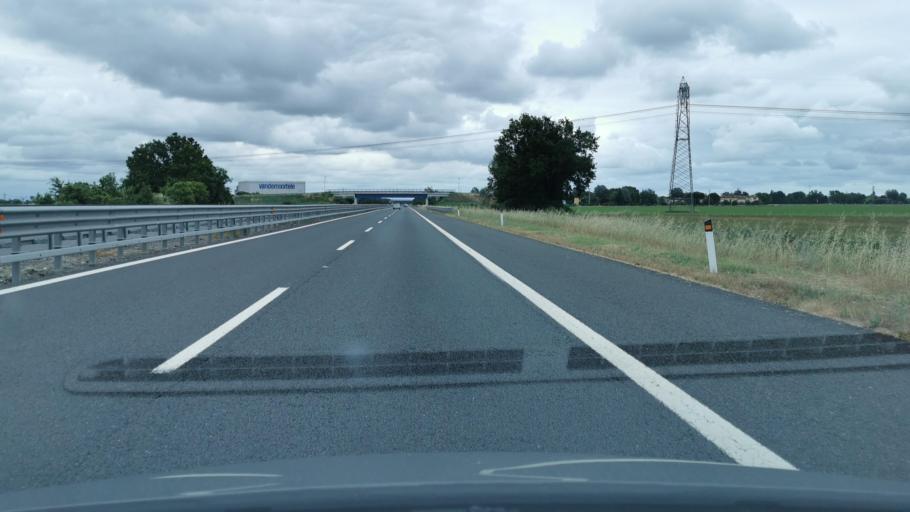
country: IT
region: Emilia-Romagna
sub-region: Provincia di Ravenna
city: Piangipane
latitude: 44.4088
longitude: 12.0984
